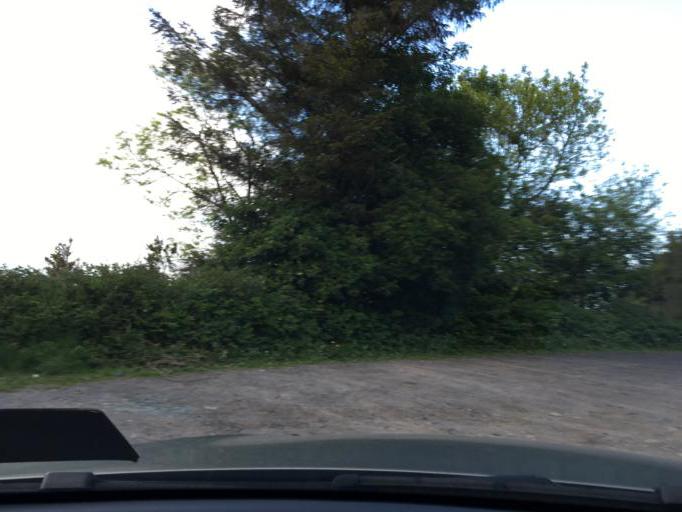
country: IE
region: Leinster
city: Ballinteer
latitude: 53.2583
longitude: -6.2760
